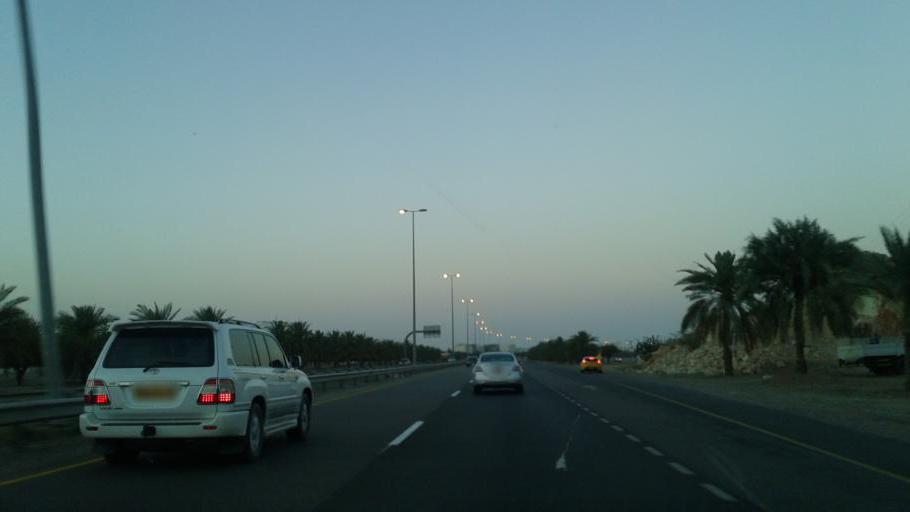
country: OM
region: Muhafazat Masqat
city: As Sib al Jadidah
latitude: 23.5815
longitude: 58.1961
